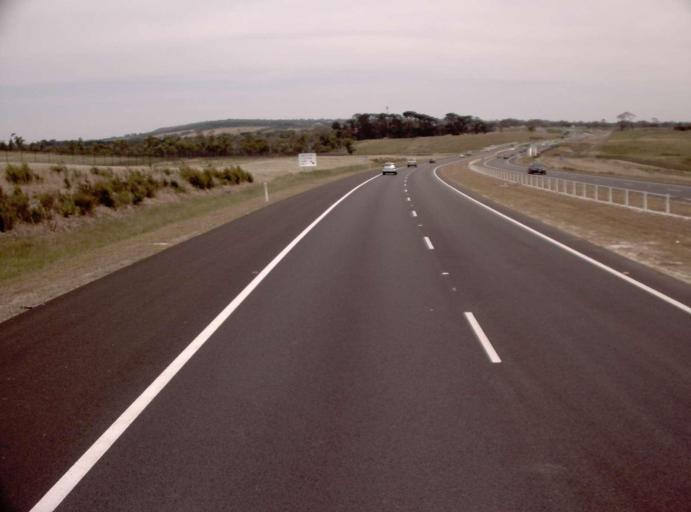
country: AU
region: Victoria
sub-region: Mornington Peninsula
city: Moorooduc
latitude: -38.2712
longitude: 145.0870
